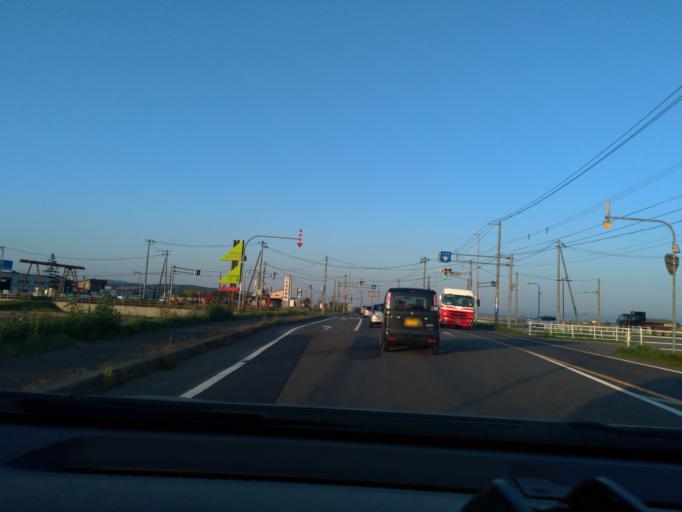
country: JP
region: Hokkaido
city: Tobetsu
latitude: 43.2152
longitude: 141.5294
